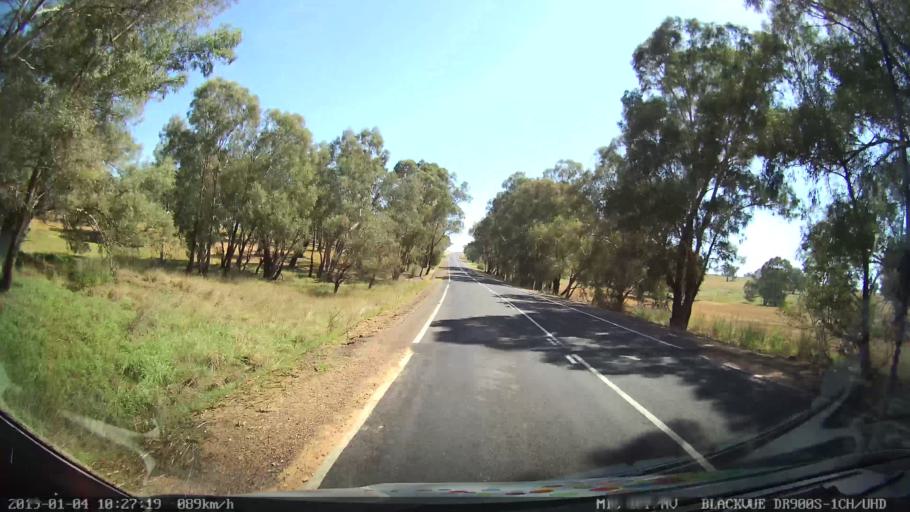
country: AU
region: New South Wales
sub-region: Cabonne
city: Canowindra
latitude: -33.3718
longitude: 148.5977
